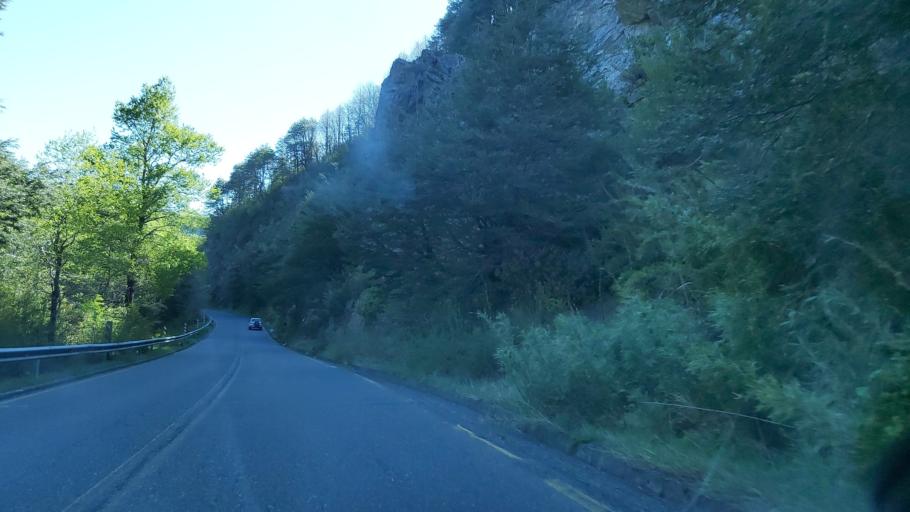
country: CL
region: Araucania
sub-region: Provincia de Cautin
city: Vilcun
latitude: -38.4687
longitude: -71.6423
